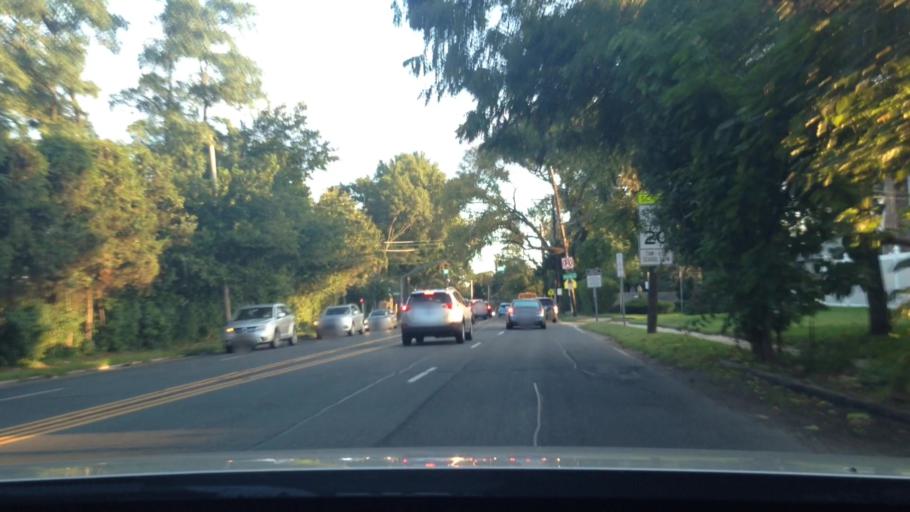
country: US
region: New York
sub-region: Nassau County
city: Lakeview
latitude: 40.6836
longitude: -73.6630
